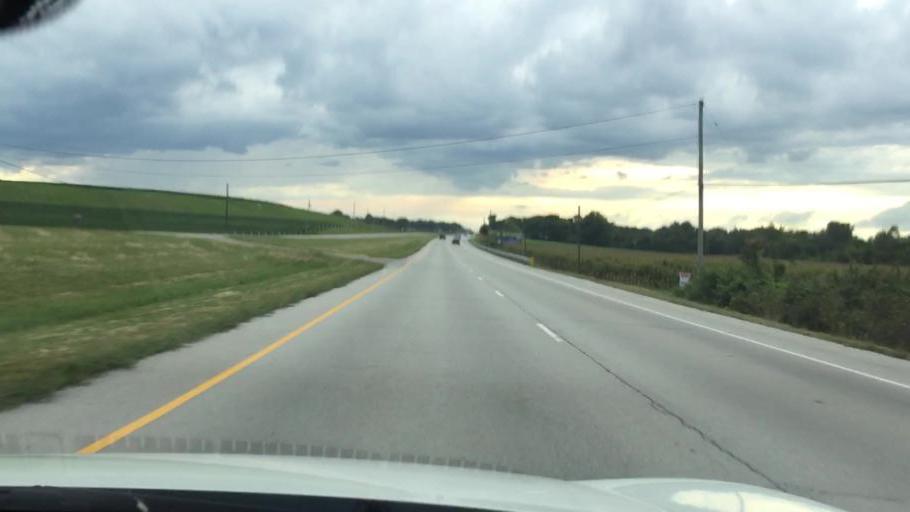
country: US
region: Ohio
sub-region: Clark County
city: Lisbon
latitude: 39.9233
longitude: -83.7095
